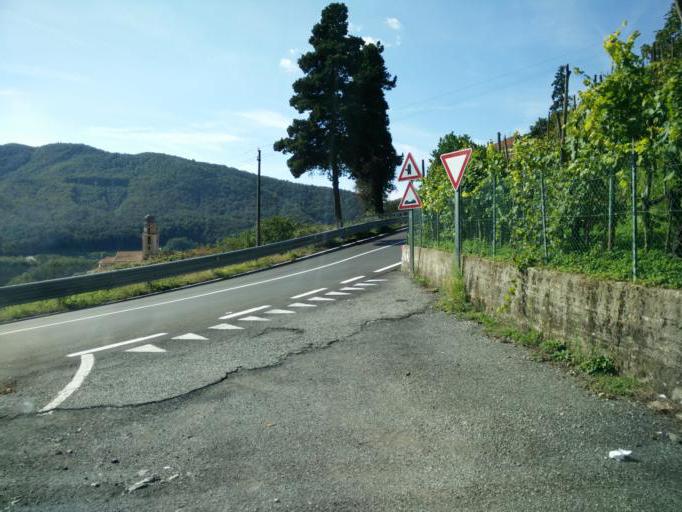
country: IT
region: Liguria
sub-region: Provincia di La Spezia
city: Carrodano
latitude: 44.2435
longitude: 9.6570
